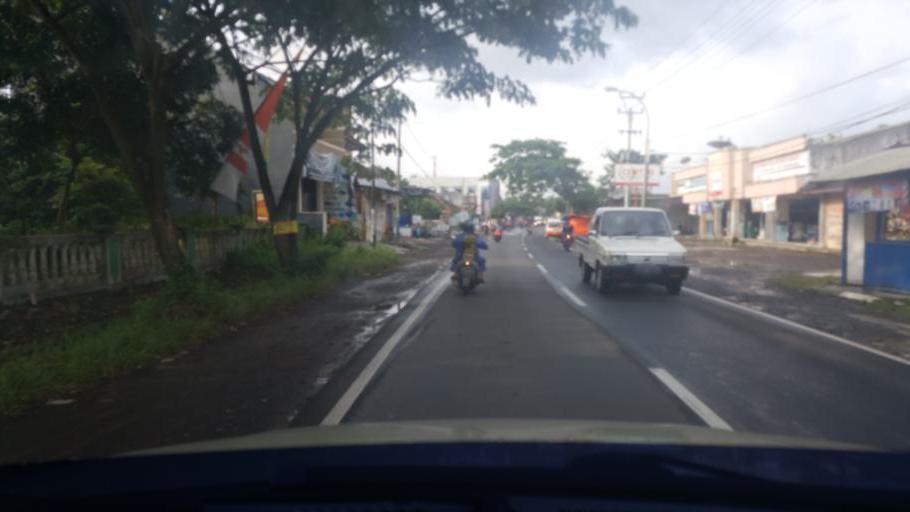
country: ID
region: West Java
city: Pakemitan
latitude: -7.2967
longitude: 108.2002
